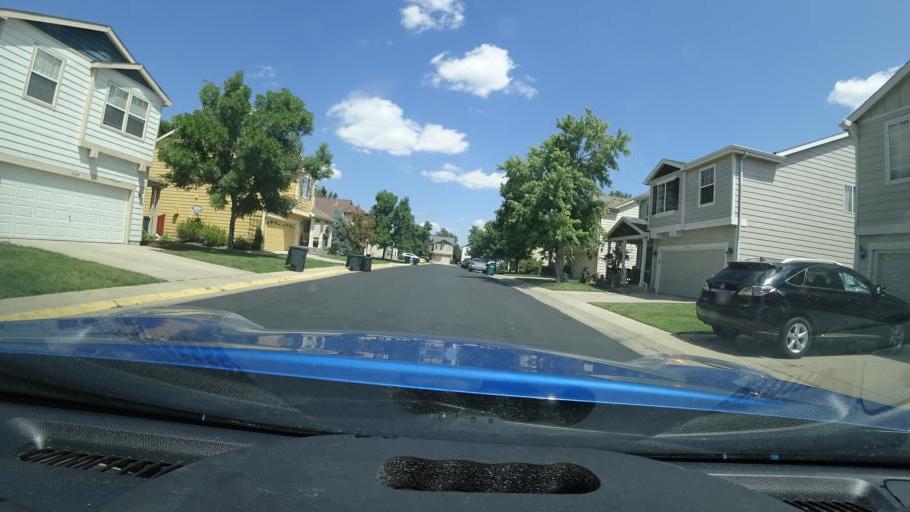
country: US
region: Colorado
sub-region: Arapahoe County
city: Glendale
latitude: 39.6950
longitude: -104.8790
